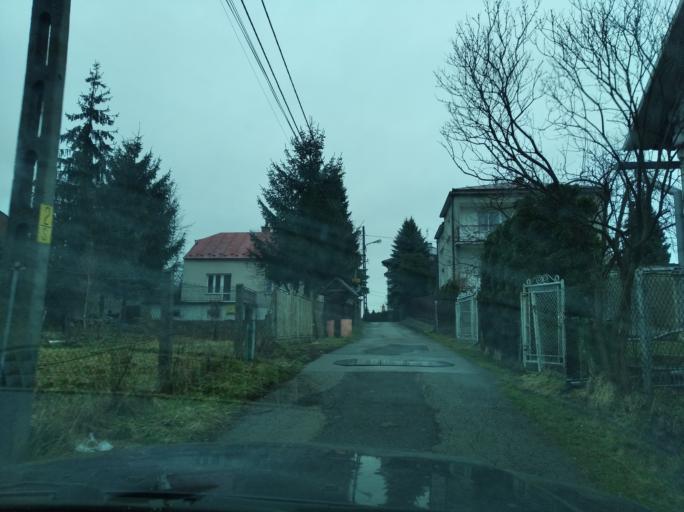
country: PL
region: Subcarpathian Voivodeship
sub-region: Rzeszow
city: Rzeszow
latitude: 50.0584
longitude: 22.0019
